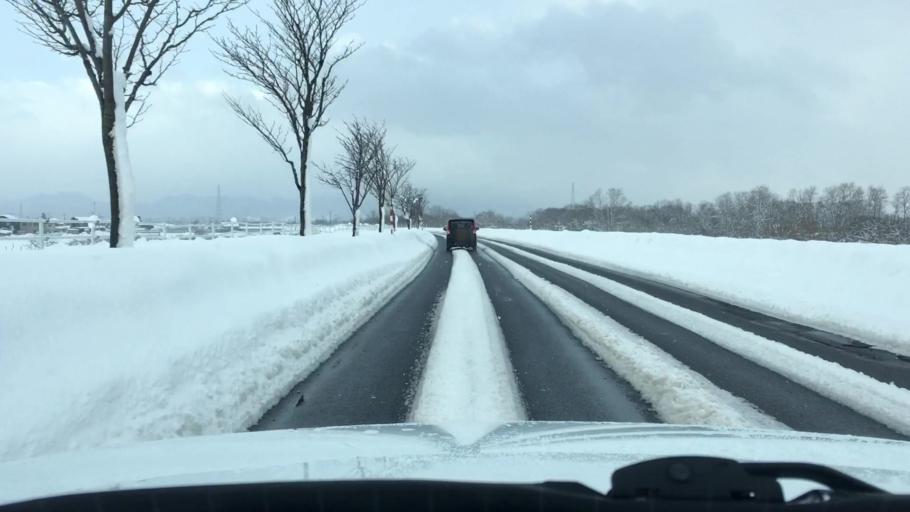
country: JP
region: Aomori
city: Hirosaki
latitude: 40.6386
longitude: 140.4717
